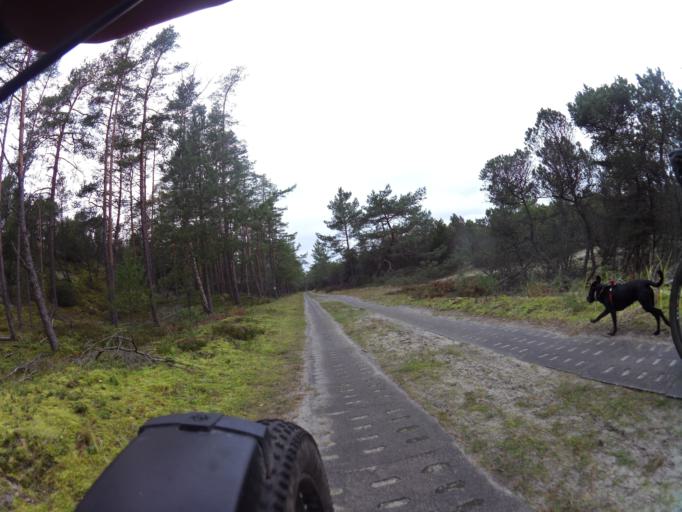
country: PL
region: Pomeranian Voivodeship
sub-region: Powiat pucki
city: Hel
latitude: 54.6272
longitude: 18.8143
